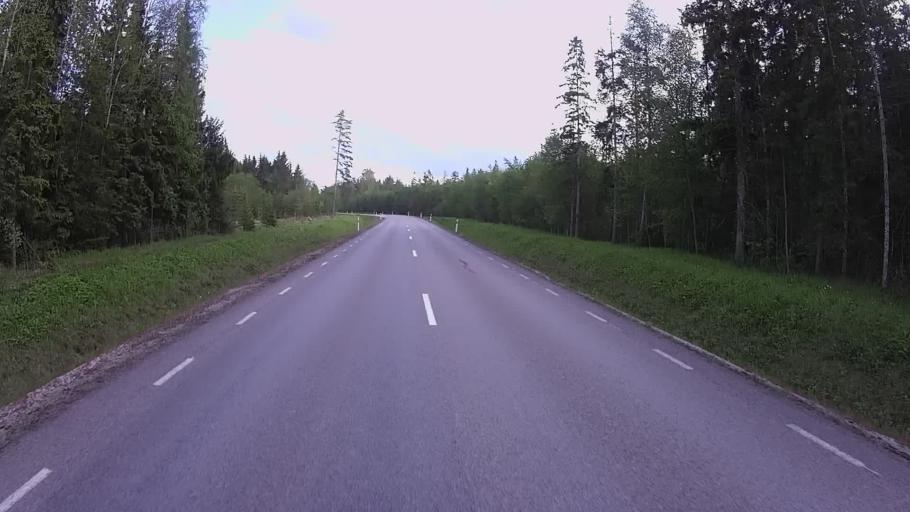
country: EE
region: Jogevamaa
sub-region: Mustvee linn
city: Mustvee
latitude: 59.0631
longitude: 27.0029
